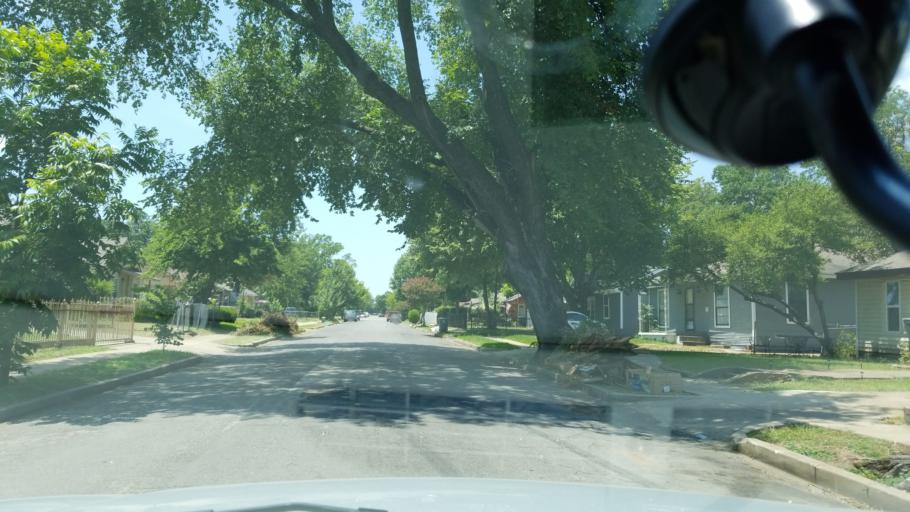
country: US
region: Texas
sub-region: Dallas County
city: Cockrell Hill
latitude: 32.7311
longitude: -96.8598
